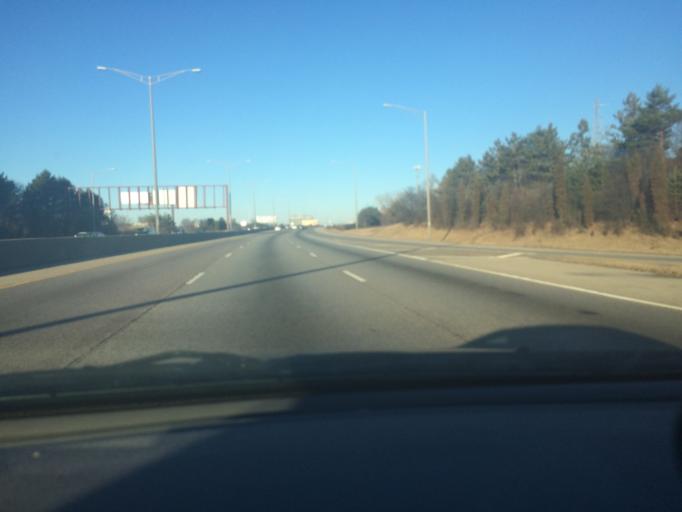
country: US
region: Illinois
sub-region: Cook County
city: Rolling Meadows
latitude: 42.0910
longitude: -88.0301
